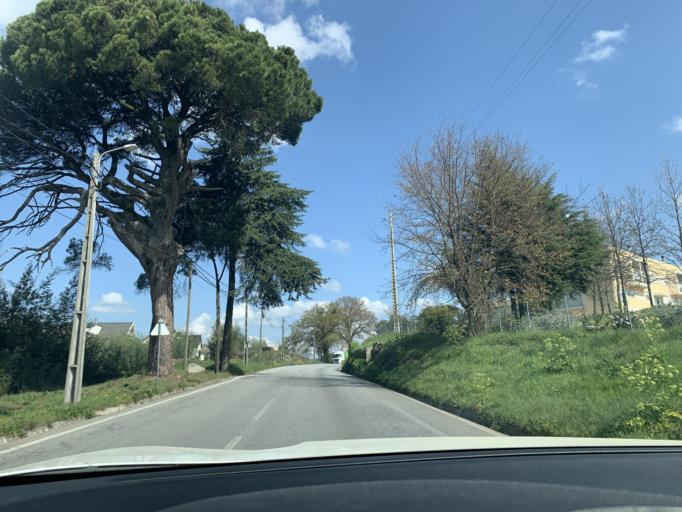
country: PT
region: Viseu
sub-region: Viseu
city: Rio de Loba
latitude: 40.6942
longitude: -7.8737
